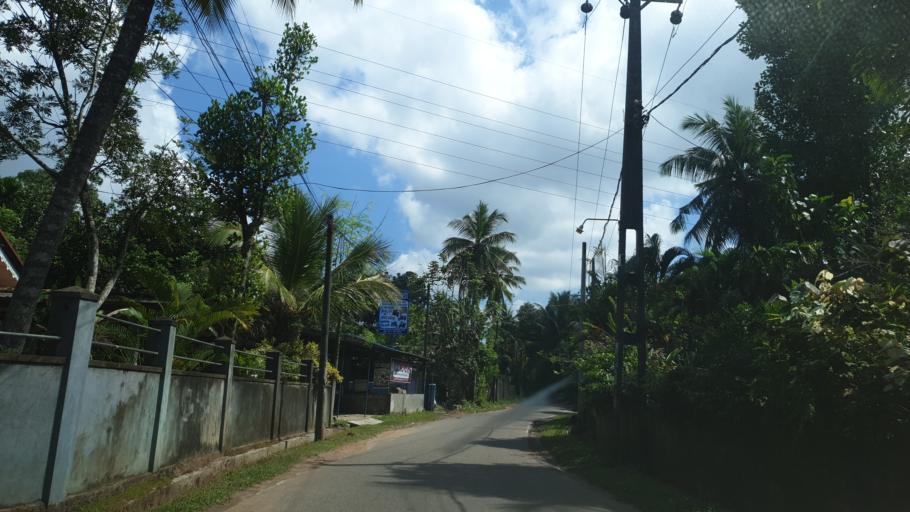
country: LK
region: Western
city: Panadura
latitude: 6.6741
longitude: 79.9372
